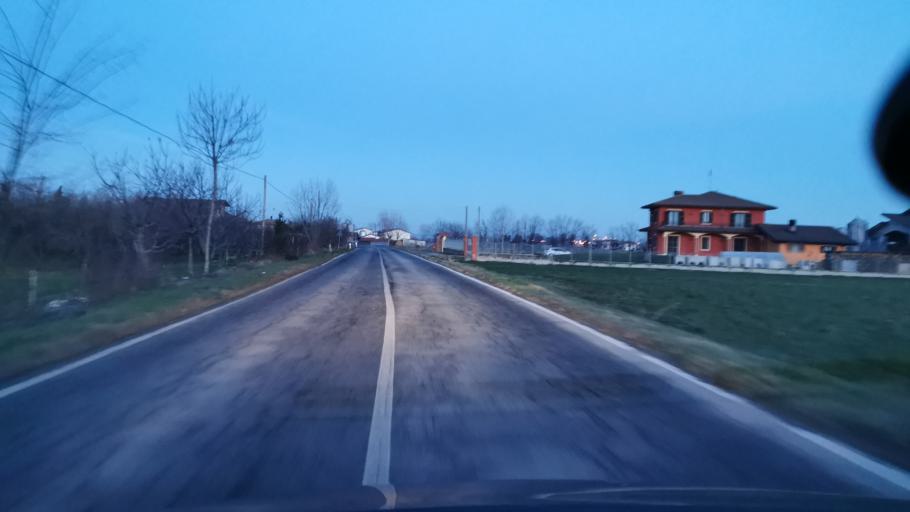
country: IT
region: Piedmont
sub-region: Provincia di Cuneo
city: Roata Rossi
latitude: 44.4400
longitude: 7.5493
